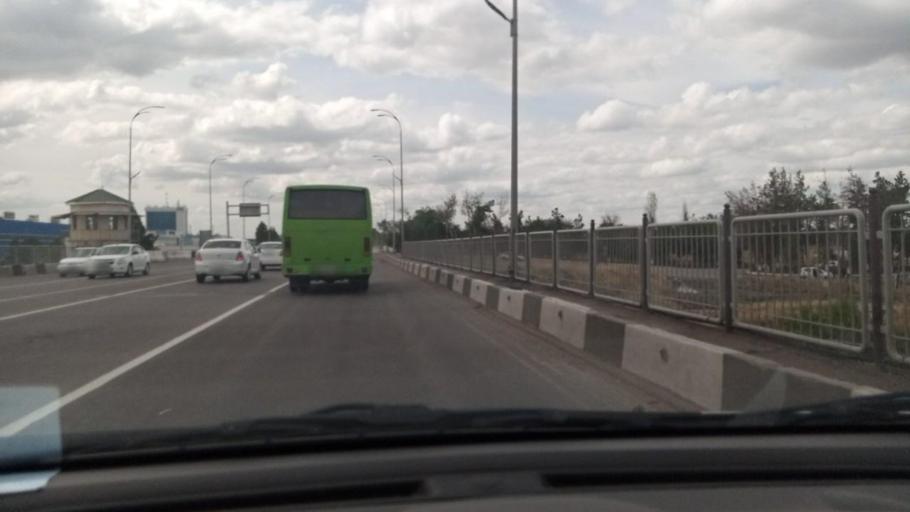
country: UZ
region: Toshkent Shahri
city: Bektemir
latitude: 41.2617
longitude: 69.3750
